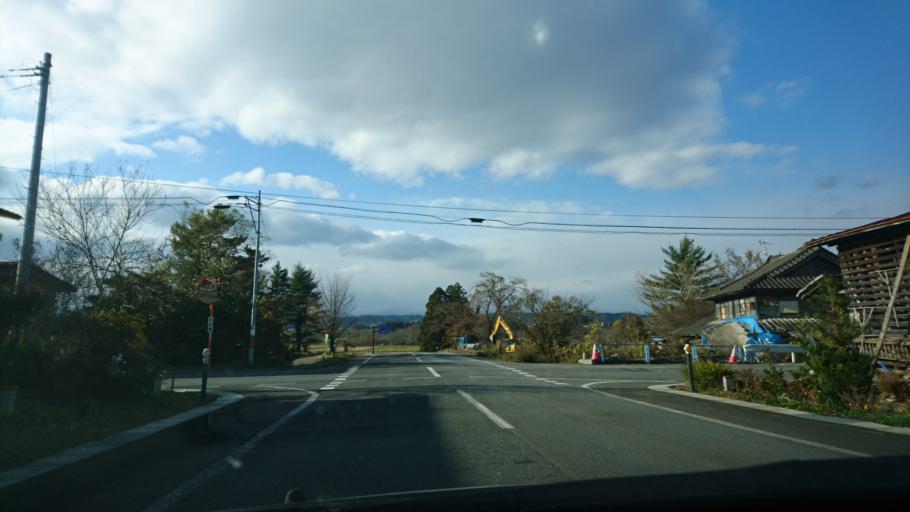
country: JP
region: Iwate
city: Mizusawa
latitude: 39.0353
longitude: 141.1528
